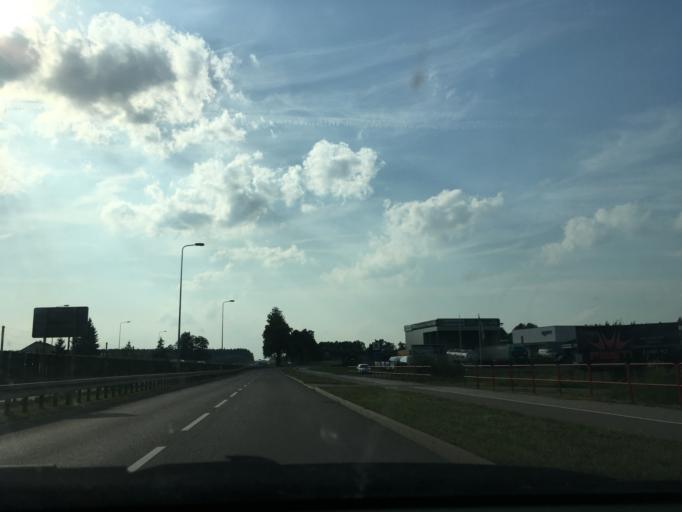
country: PL
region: Podlasie
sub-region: Powiat bialostocki
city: Choroszcz
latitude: 53.1520
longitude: 23.0407
